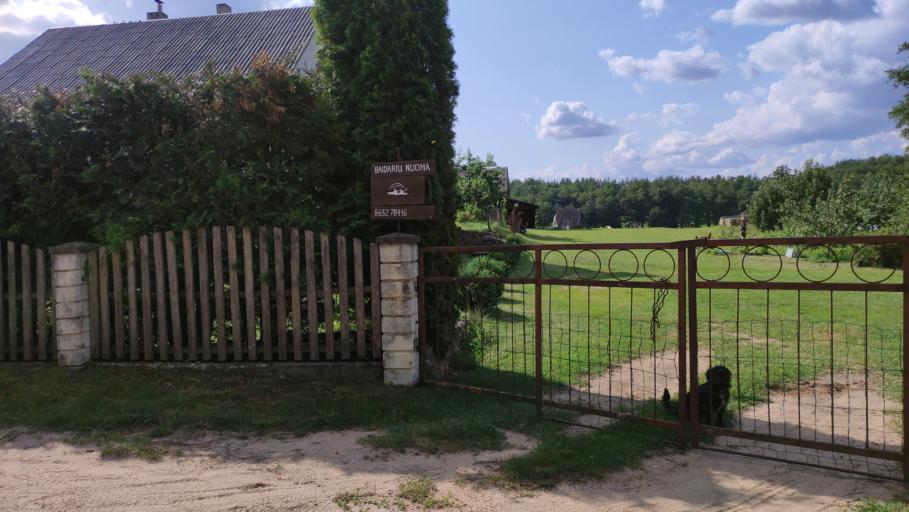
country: LT
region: Alytaus apskritis
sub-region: Alytus
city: Alytus
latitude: 54.4351
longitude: 24.0737
